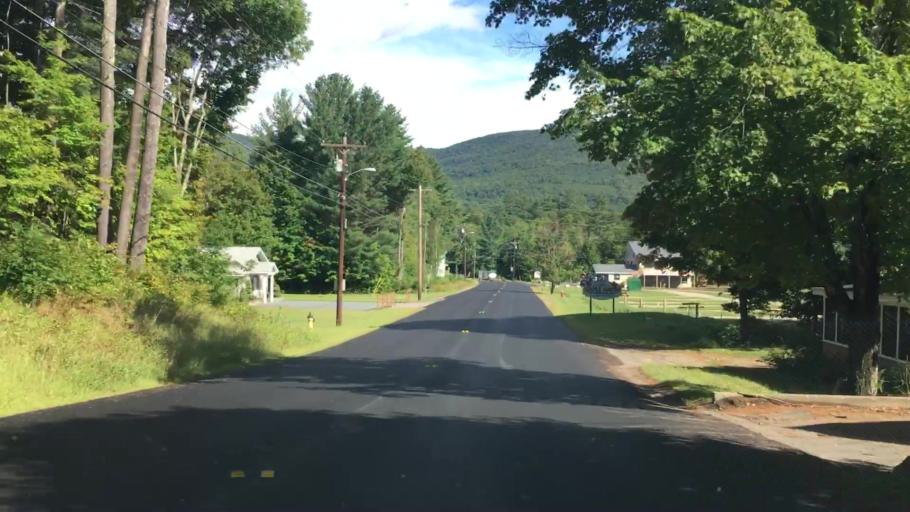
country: US
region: New Hampshire
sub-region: Grafton County
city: Woodstock
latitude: 44.0321
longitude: -71.6956
